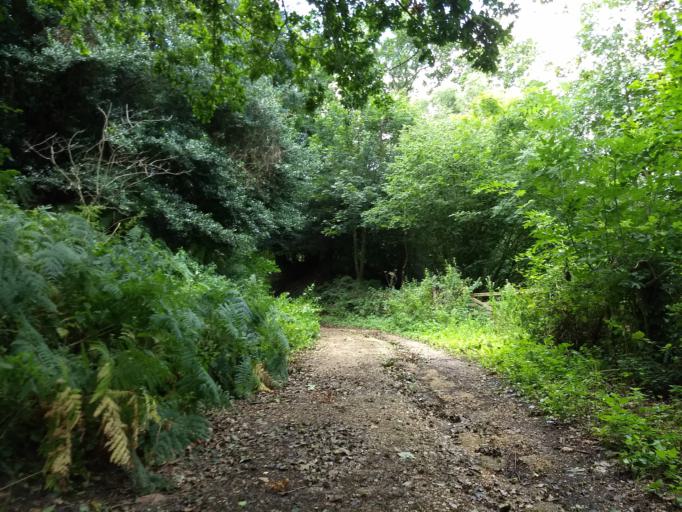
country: GB
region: England
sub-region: Isle of Wight
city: Newport
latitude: 50.6797
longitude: -1.2971
